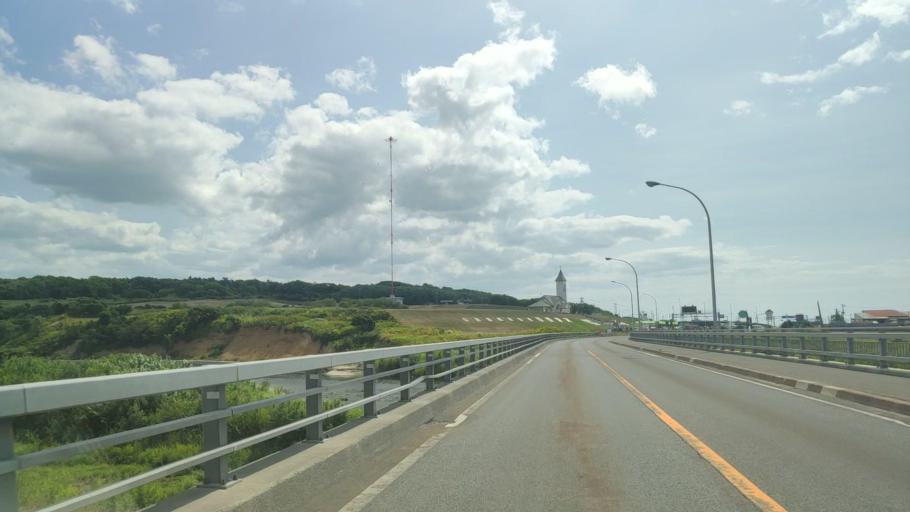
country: JP
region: Hokkaido
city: Makubetsu
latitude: 44.7175
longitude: 141.7932
